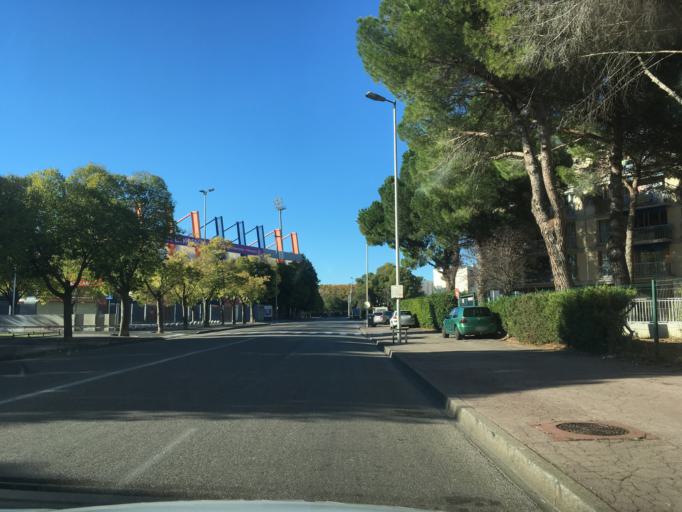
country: FR
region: Languedoc-Roussillon
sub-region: Departement de l'Herault
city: Juvignac
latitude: 43.6219
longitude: 3.8144
